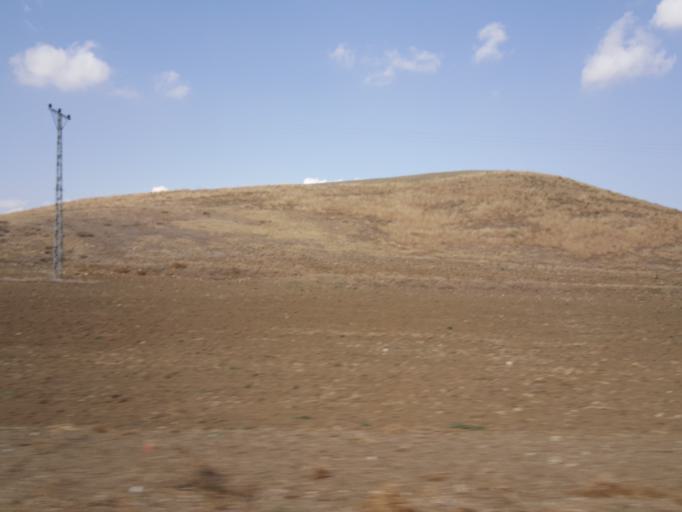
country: TR
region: Corum
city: Bogazkale
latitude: 40.1479
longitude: 34.5835
